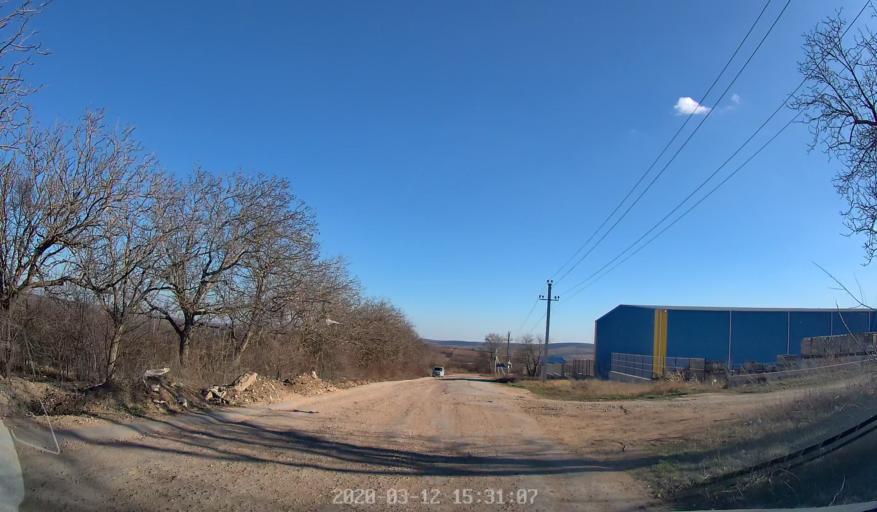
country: MD
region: Chisinau
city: Ciorescu
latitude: 47.1583
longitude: 28.9417
